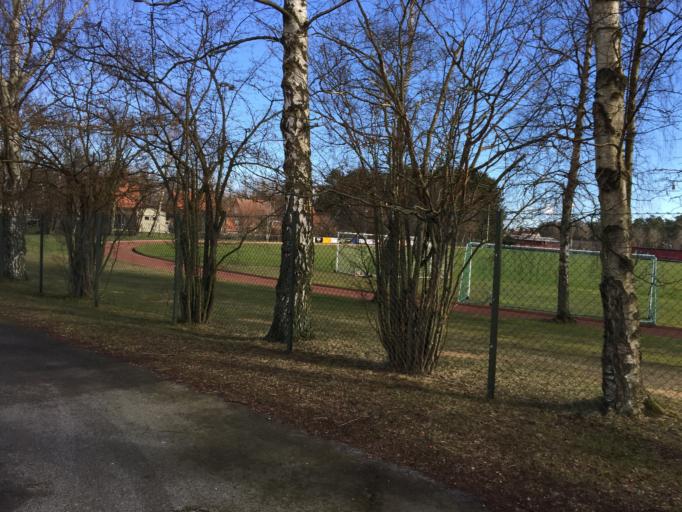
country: SE
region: Skane
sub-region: Lunds Kommun
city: Veberod
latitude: 55.6333
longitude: 13.4989
